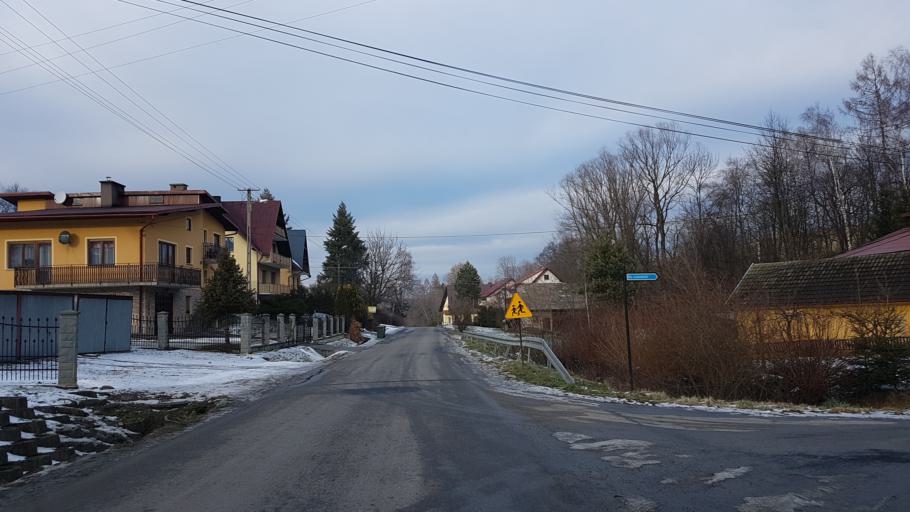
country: PL
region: Lesser Poland Voivodeship
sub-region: Powiat nowosadecki
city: Stary Sacz
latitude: 49.5212
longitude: 20.6087
